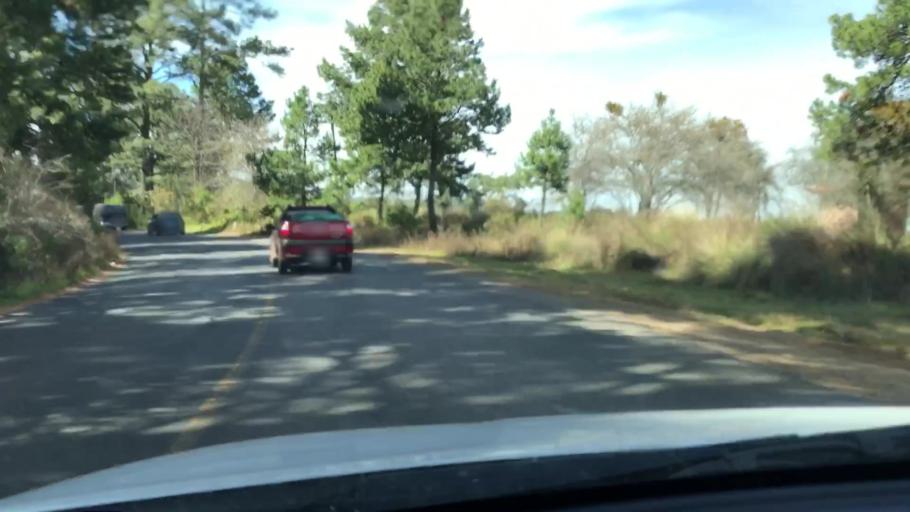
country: MX
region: Jalisco
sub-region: Amacueca
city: Tepec
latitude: 20.0807
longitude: -103.7124
